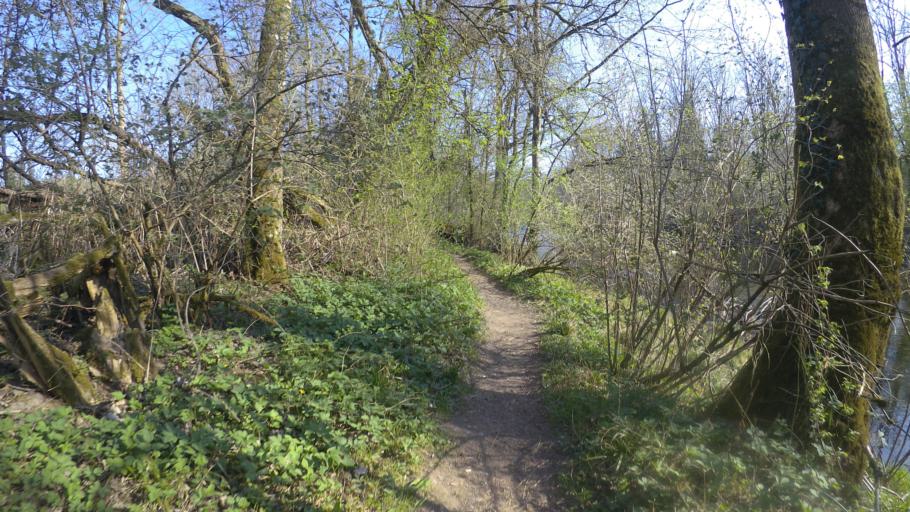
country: DE
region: Bavaria
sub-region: Upper Bavaria
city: Traunreut
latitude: 47.9518
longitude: 12.5858
